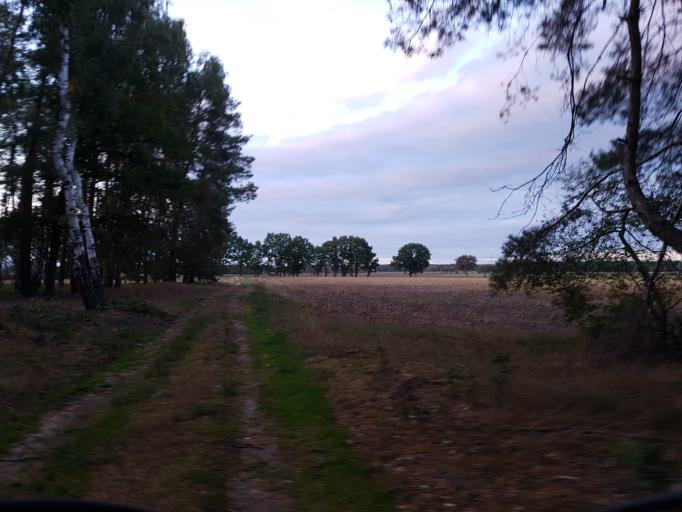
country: DE
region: Brandenburg
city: Schilda
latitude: 51.6062
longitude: 13.3637
